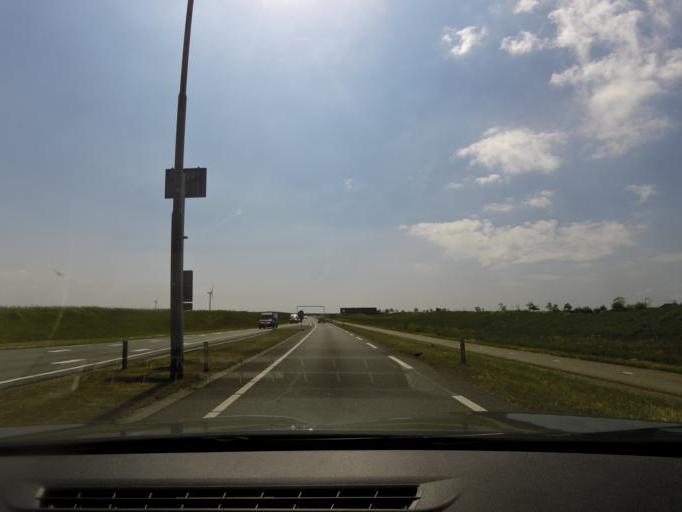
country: NL
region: Zeeland
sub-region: Schouwen-Duiveland
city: Scharendijke
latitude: 51.6463
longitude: 3.9399
